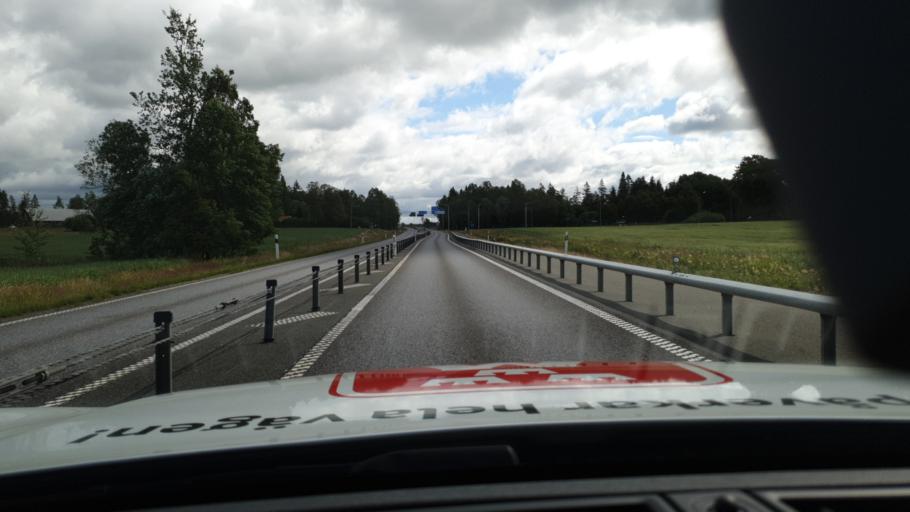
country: SE
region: Joenkoeping
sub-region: Varnamo Kommun
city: Rydaholm
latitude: 56.8740
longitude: 14.1692
